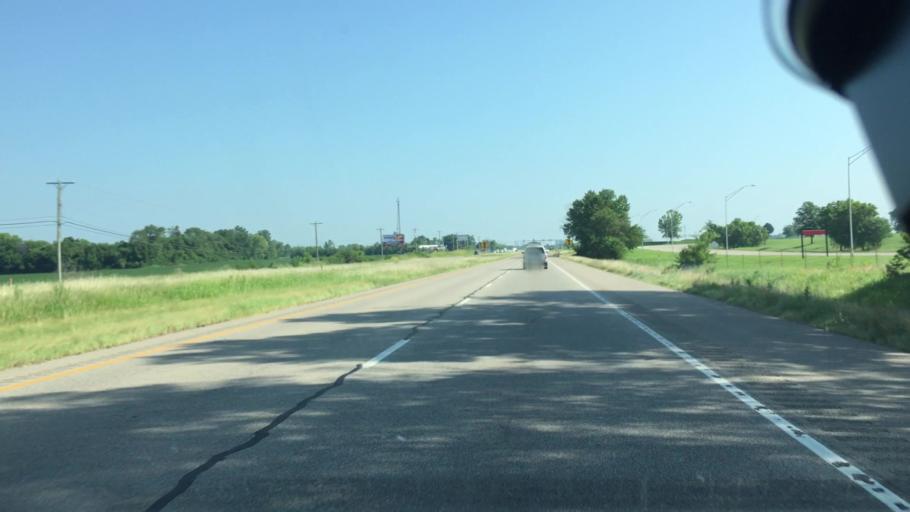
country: US
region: Indiana
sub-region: Gibson County
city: Fort Branch
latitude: 38.2985
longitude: -87.5674
